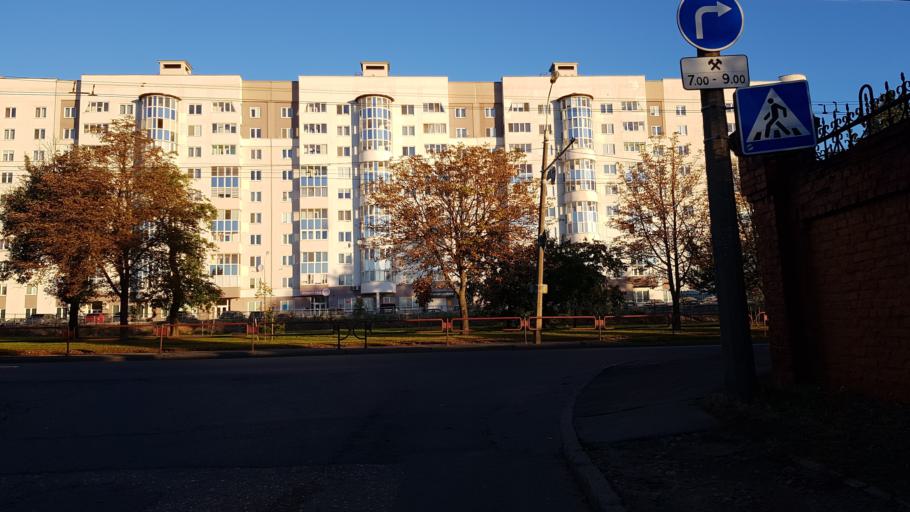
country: BY
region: Minsk
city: Syenitsa
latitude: 53.8797
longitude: 27.5201
